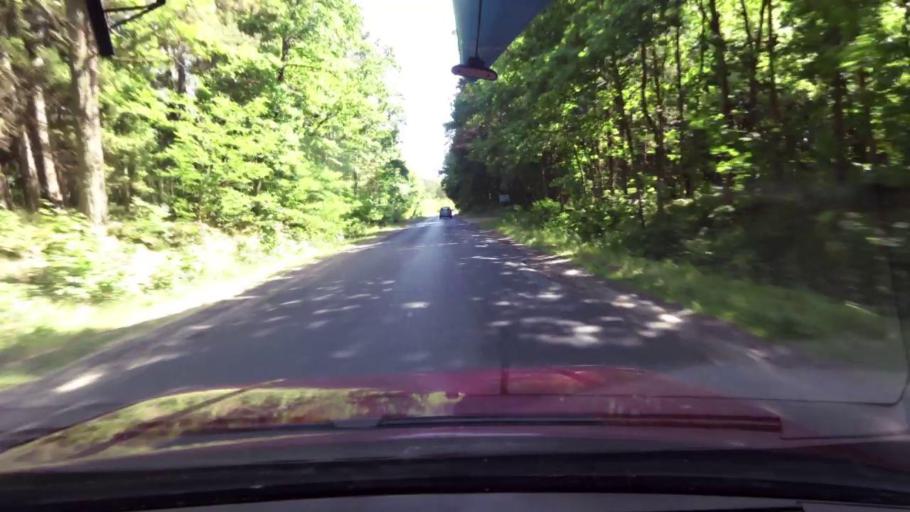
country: PL
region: Pomeranian Voivodeship
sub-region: Powiat slupski
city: Kepice
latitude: 54.2905
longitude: 16.9605
